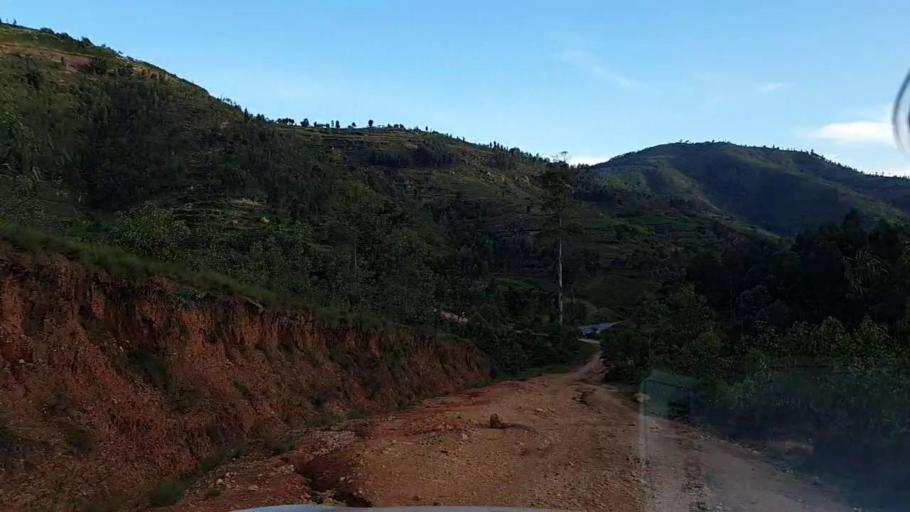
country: RW
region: Southern Province
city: Gikongoro
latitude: -2.4018
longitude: 29.5656
